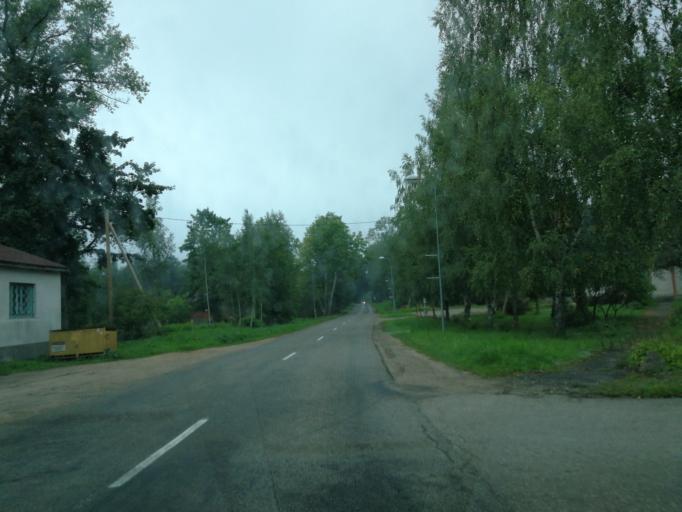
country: LV
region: Preilu Rajons
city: Jaunaglona
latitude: 56.2726
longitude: 27.0432
